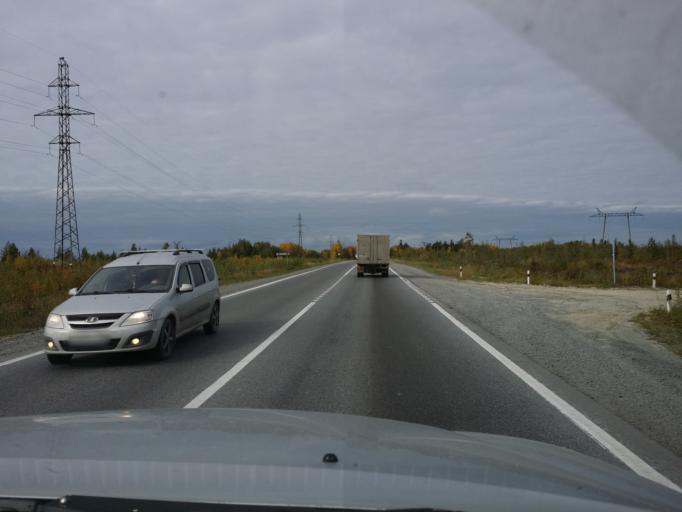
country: RU
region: Khanty-Mansiyskiy Avtonomnyy Okrug
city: Megion
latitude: 61.1039
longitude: 75.9416
